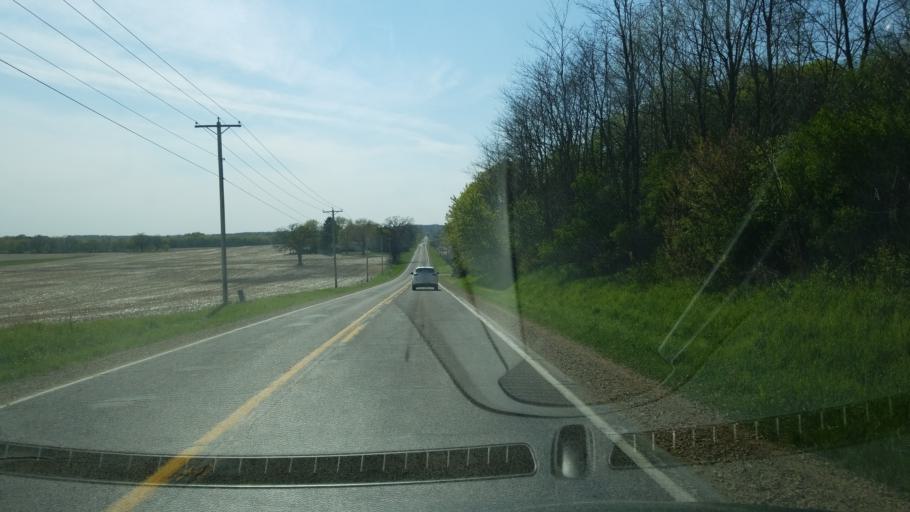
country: US
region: Wisconsin
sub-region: Dane County
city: Oregon
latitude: 42.9291
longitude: -89.4198
